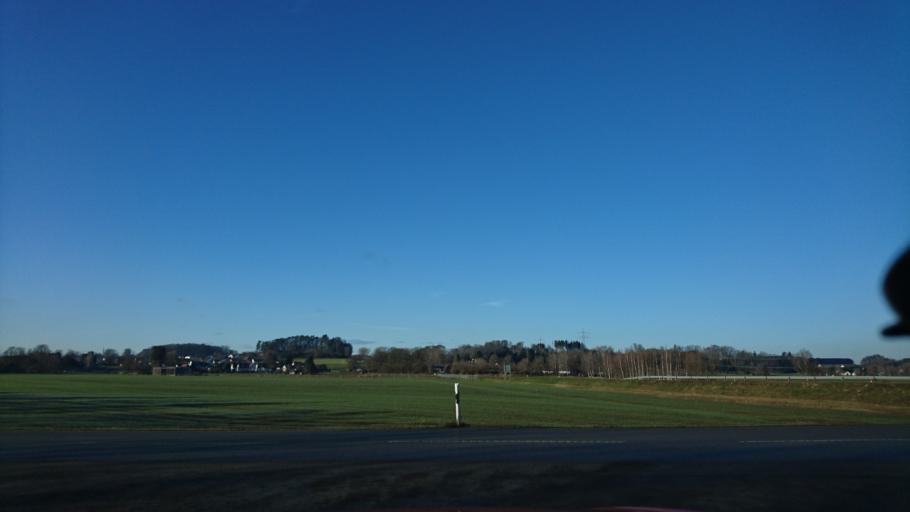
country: DE
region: Bavaria
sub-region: Swabia
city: Biberbach
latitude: 48.5239
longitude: 10.8224
